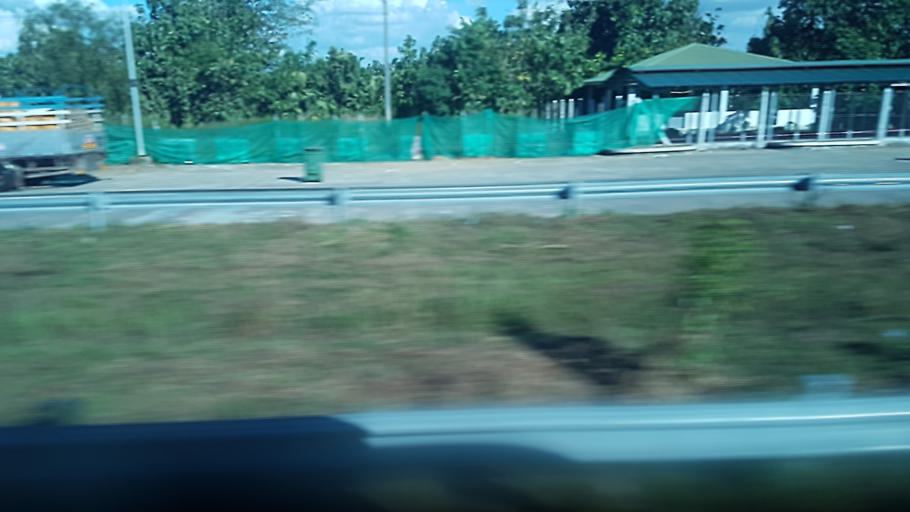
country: MM
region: Bago
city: Nyaunglebin
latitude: 17.9720
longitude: 96.4842
